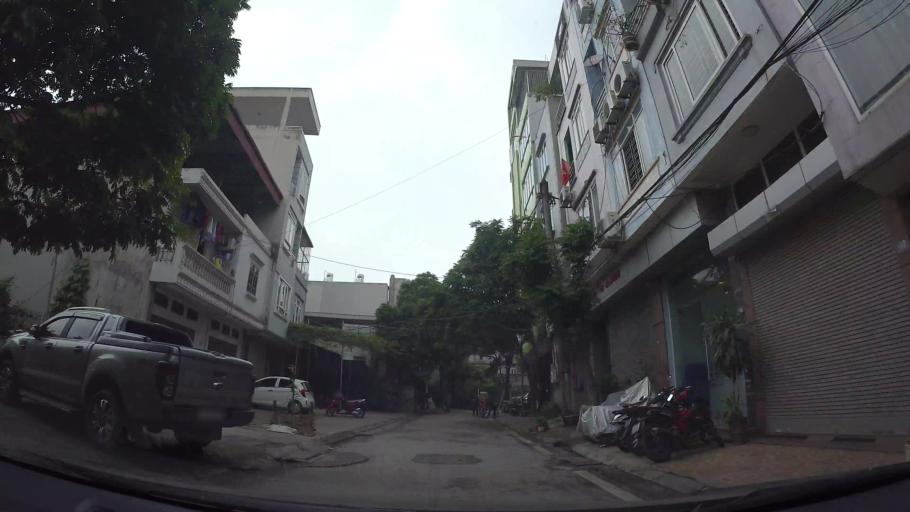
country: VN
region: Ha Noi
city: Van Dien
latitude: 20.9683
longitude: 105.8437
